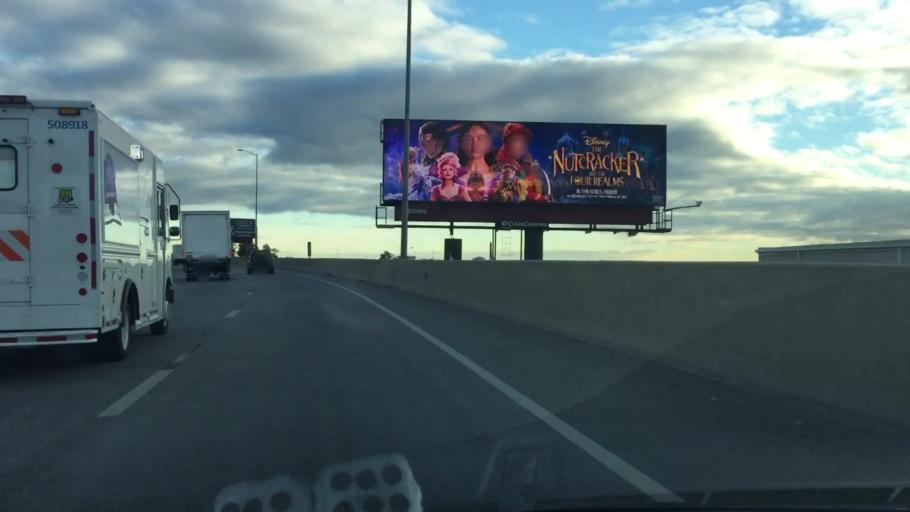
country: US
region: New Jersey
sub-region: Burlington County
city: Riverton
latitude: 40.0280
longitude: -75.0237
